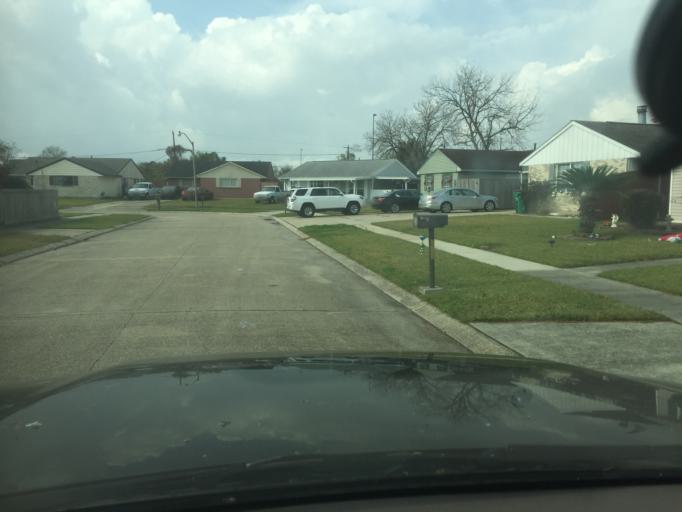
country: US
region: Louisiana
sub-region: Jefferson Parish
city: Avondale
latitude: 29.9160
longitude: -90.2029
